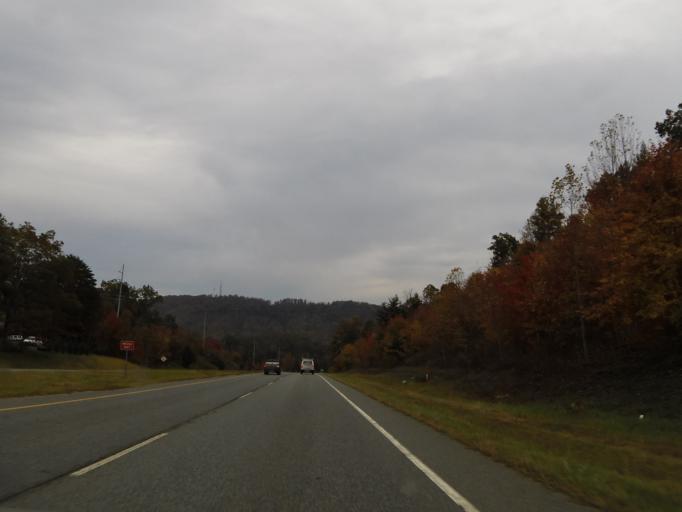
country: US
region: North Carolina
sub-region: Caldwell County
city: Lenoir
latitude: 35.9859
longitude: -81.5699
